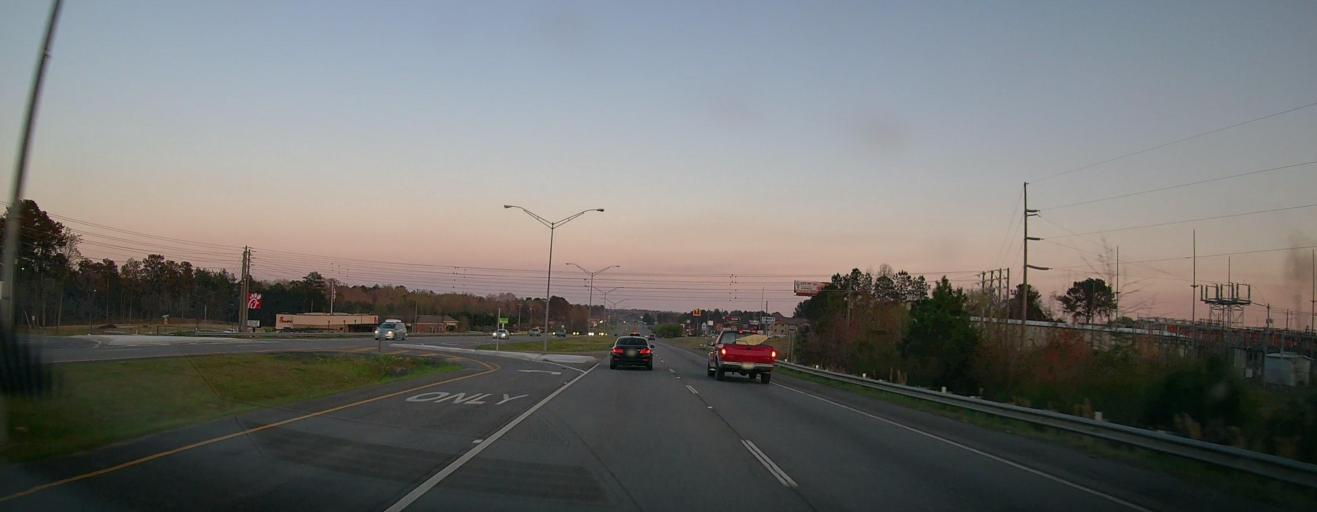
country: US
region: Alabama
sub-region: Tallapoosa County
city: Alexander City
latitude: 32.9267
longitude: -85.9637
